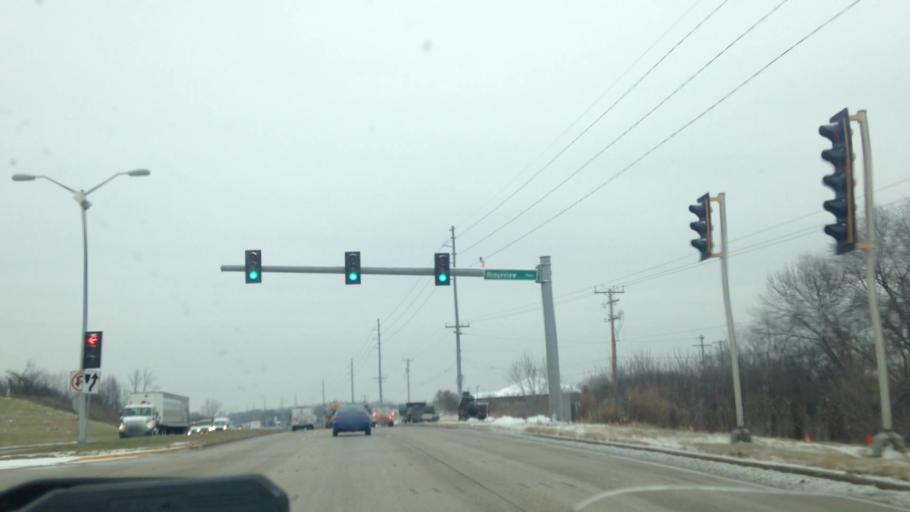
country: US
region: Wisconsin
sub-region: Waukesha County
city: Waukesha
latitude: 43.0541
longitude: -88.2061
